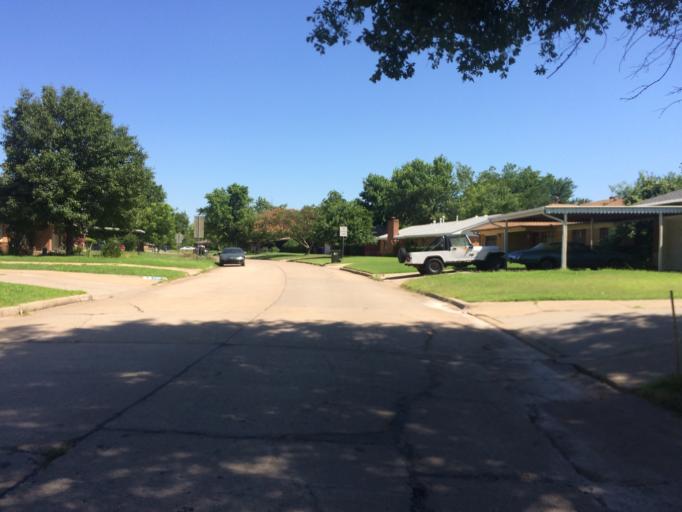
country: US
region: Oklahoma
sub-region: Cleveland County
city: Norman
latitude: 35.2293
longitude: -97.4562
